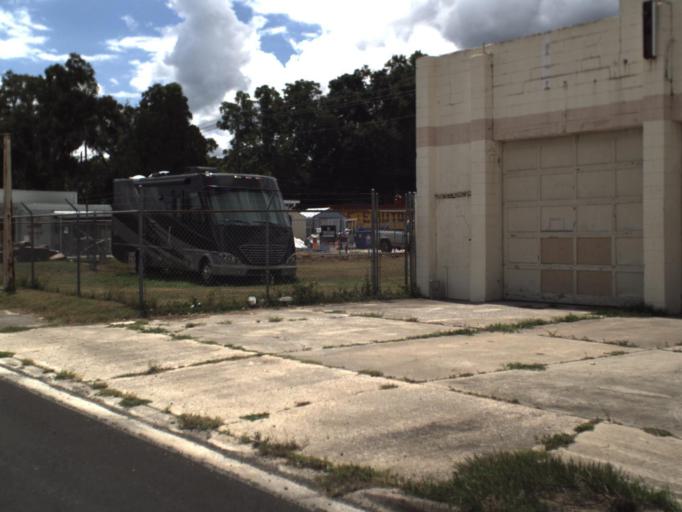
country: US
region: Florida
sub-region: Polk County
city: Highland City
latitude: 27.9644
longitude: -81.8776
